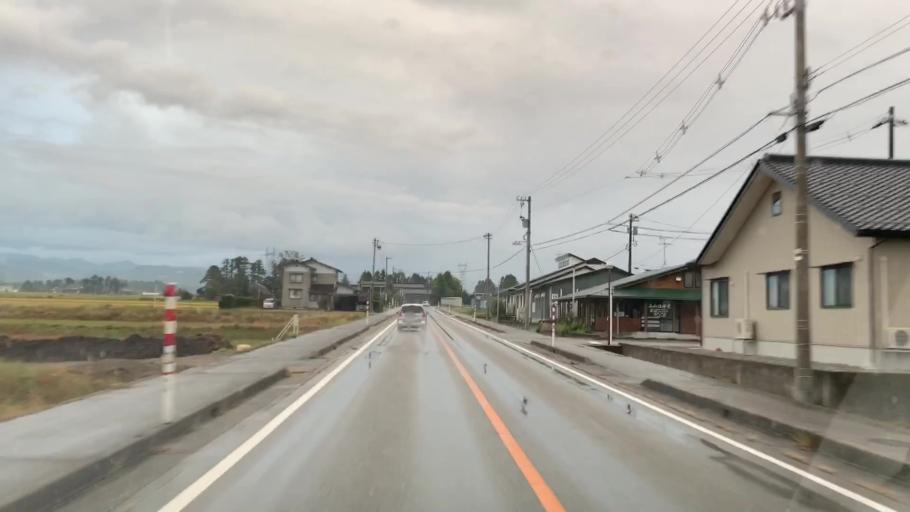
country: JP
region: Toyama
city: Kamiichi
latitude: 36.6658
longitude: 137.3276
